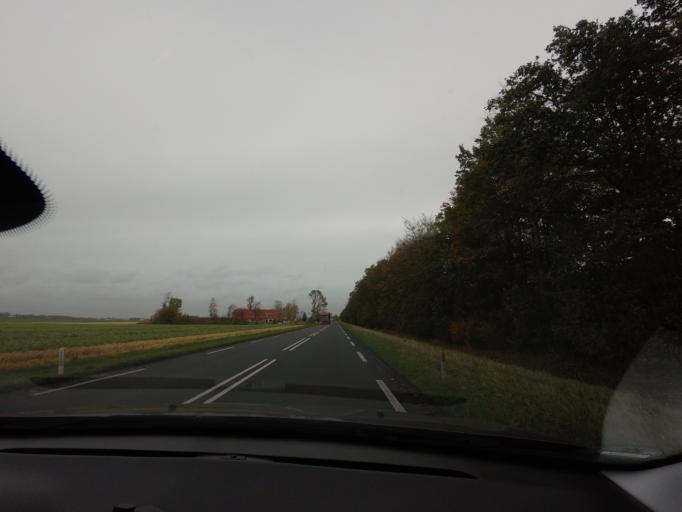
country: NL
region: Flevoland
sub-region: Gemeente Noordoostpolder
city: Ens
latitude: 52.7102
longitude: 5.8504
